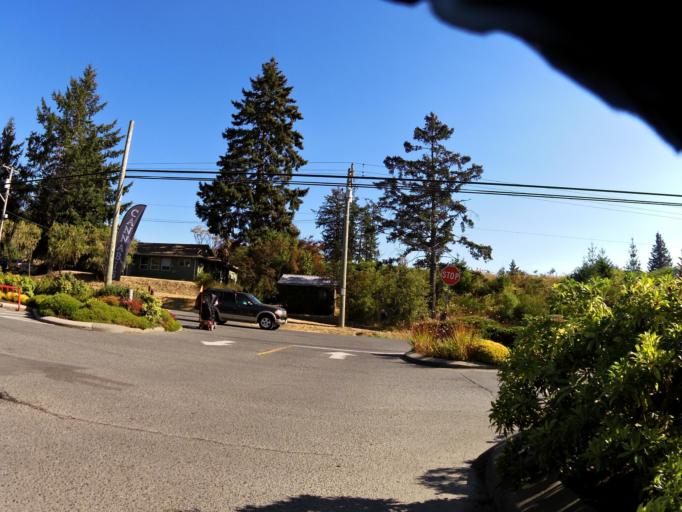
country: CA
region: British Columbia
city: North Cowichan
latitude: 48.8609
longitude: -123.5108
